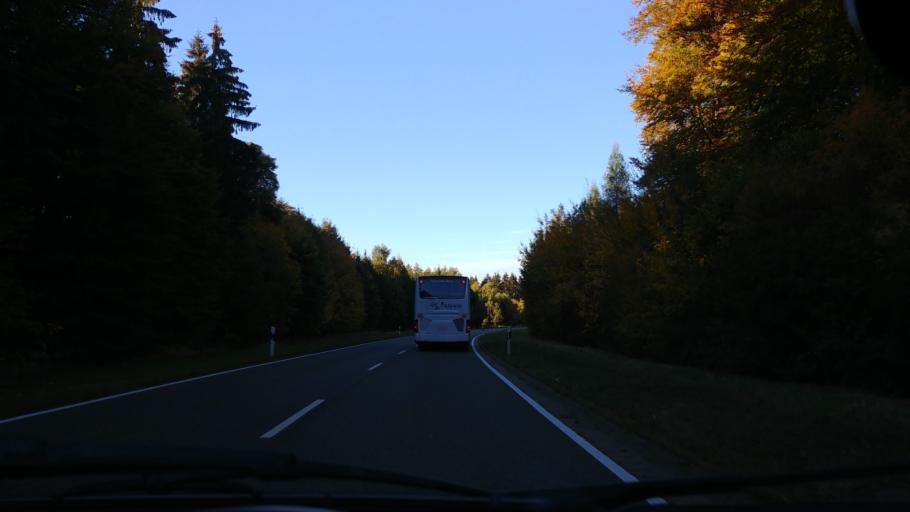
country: DE
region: Rheinland-Pfalz
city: Holzhausen an der Haide
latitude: 50.2009
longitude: 7.9050
